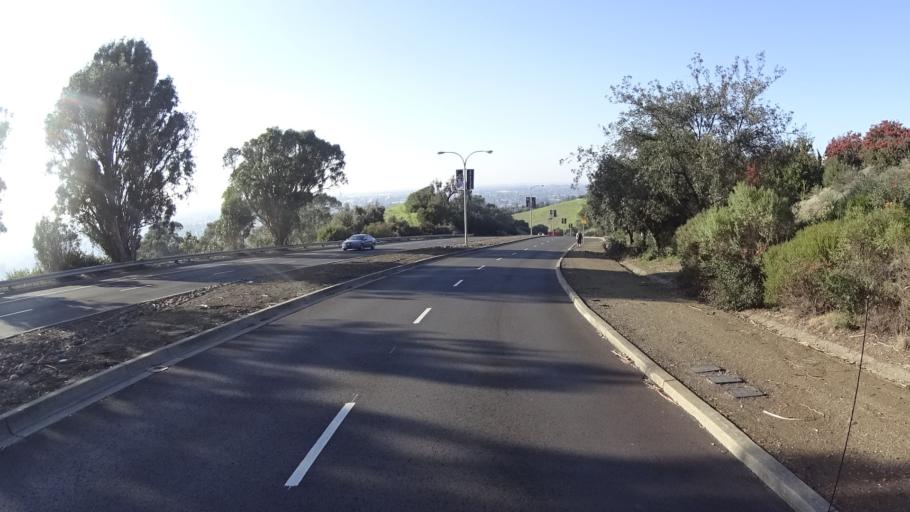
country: US
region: California
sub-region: Alameda County
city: Fairview
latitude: 37.6526
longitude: -122.0565
